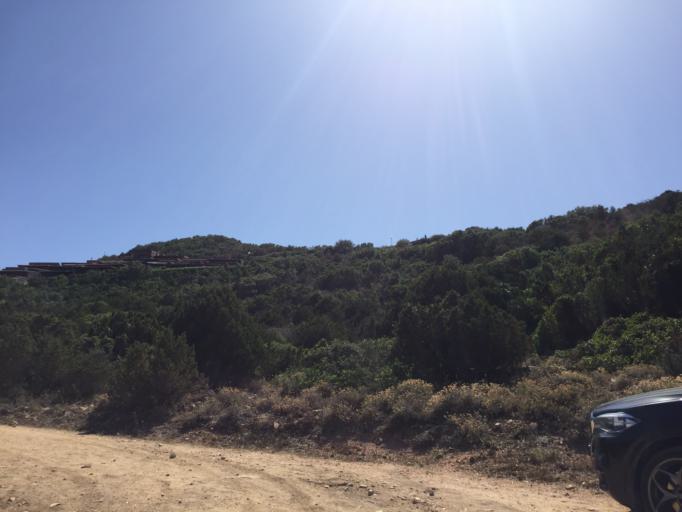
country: IT
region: Sardinia
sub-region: Provincia di Olbia-Tempio
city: San Teodoro
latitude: 40.8421
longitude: 9.7155
